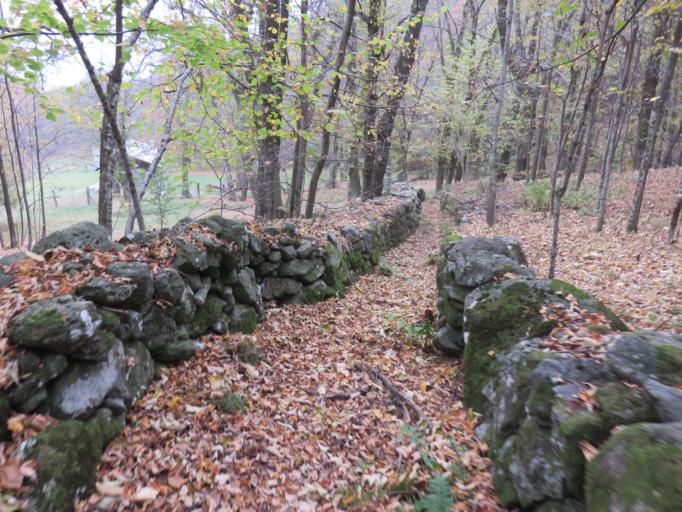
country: IT
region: Piedmont
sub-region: Provincia di Torino
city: Cantoira
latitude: 45.3487
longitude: 7.3657
